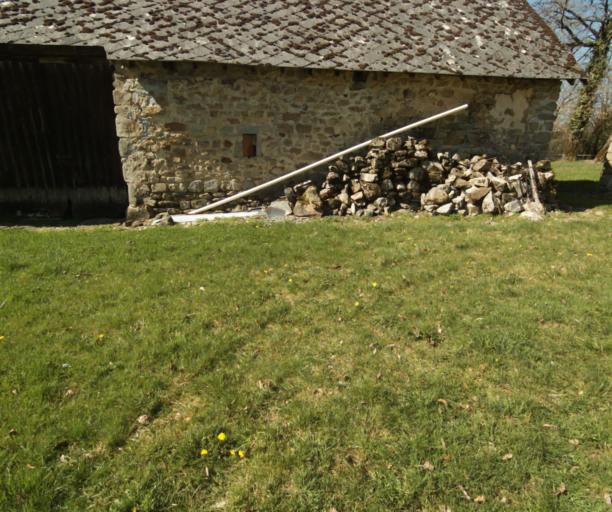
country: FR
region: Limousin
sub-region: Departement de la Correze
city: Saint-Mexant
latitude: 45.3155
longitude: 1.6438
